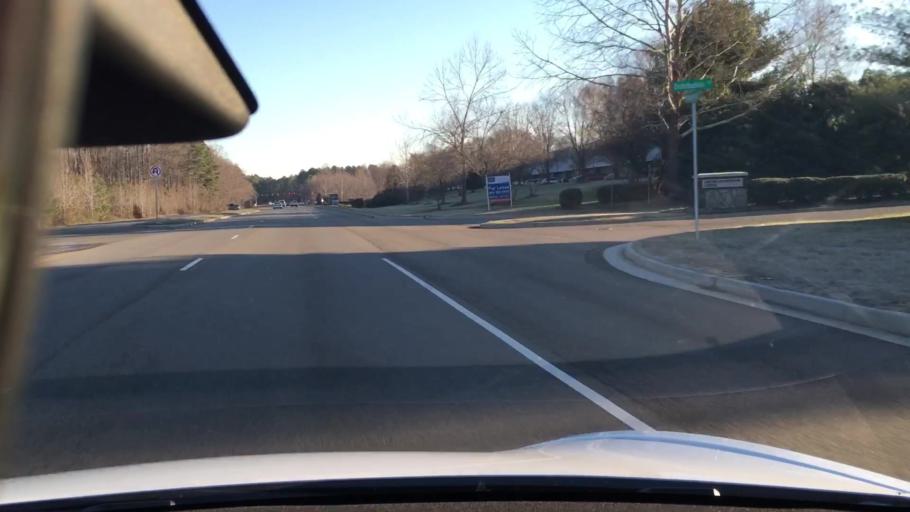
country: US
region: Virginia
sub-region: Henrico County
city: Fort Lee
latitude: 37.4790
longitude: -77.3626
